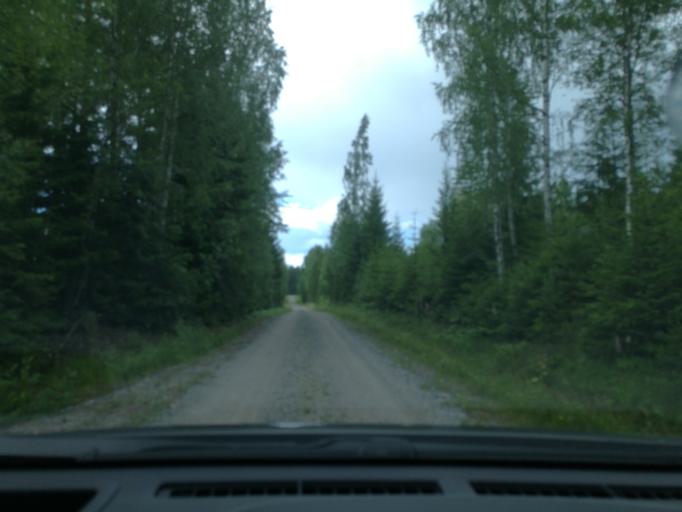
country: SE
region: Vaestmanland
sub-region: Surahammars Kommun
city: Ramnas
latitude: 59.8183
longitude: 16.2709
